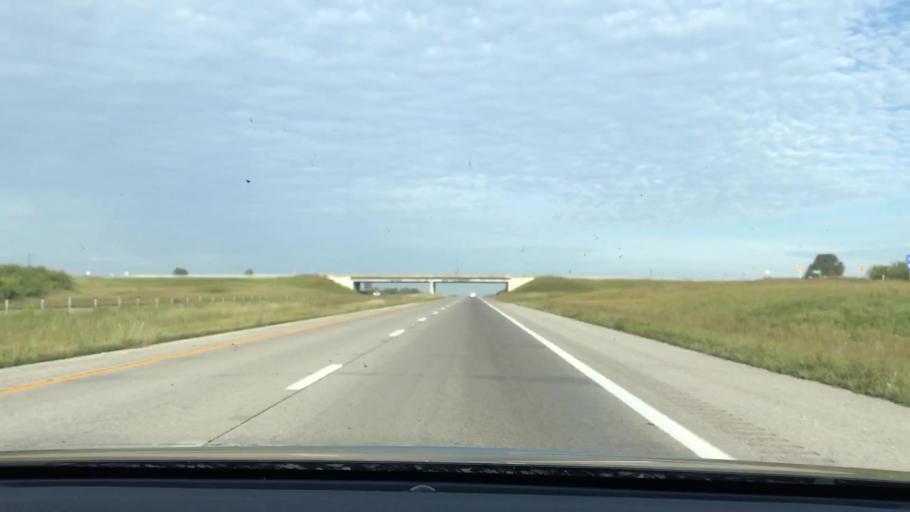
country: US
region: Kentucky
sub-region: Trigg County
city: Cadiz
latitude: 36.9657
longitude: -87.8714
